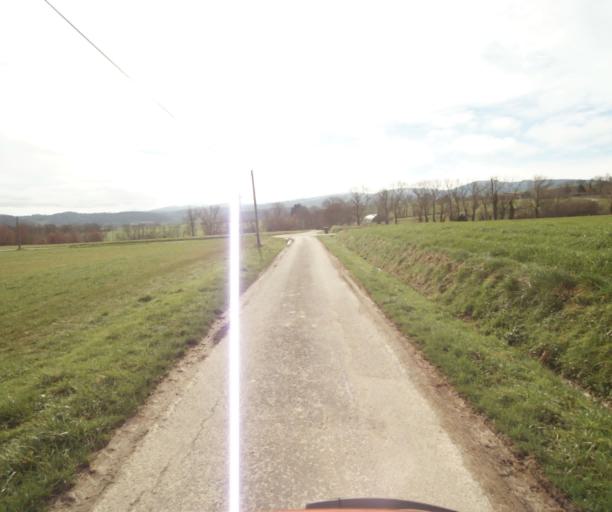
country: FR
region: Midi-Pyrenees
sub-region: Departement de l'Ariege
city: Pamiers
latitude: 43.0979
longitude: 1.5441
